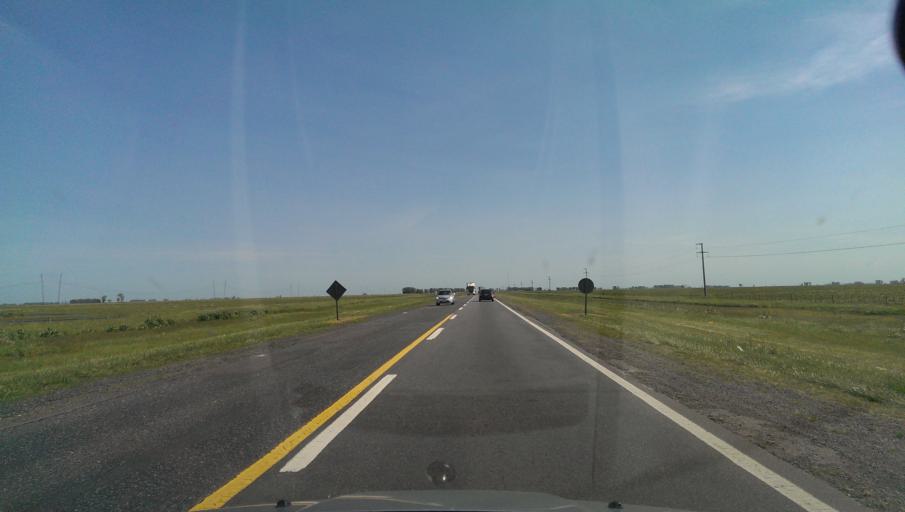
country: AR
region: Buenos Aires
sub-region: Partido de Azul
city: Azul
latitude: -36.5858
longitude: -59.6481
